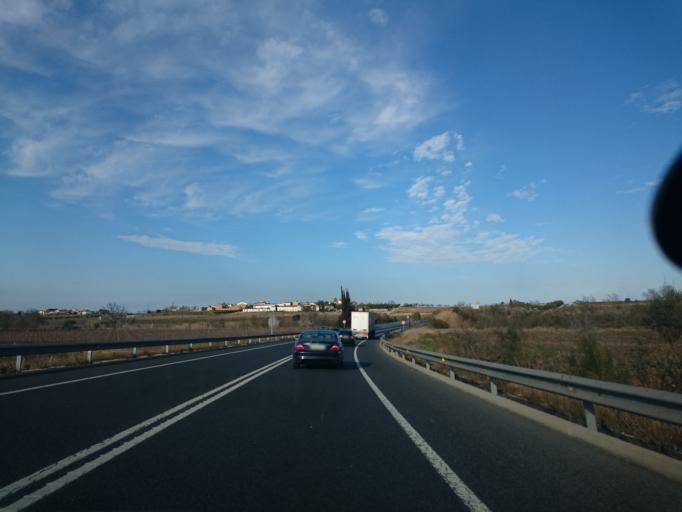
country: ES
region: Catalonia
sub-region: Provincia de Barcelona
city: Vilobi del Penedes
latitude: 41.3267
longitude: 1.6452
